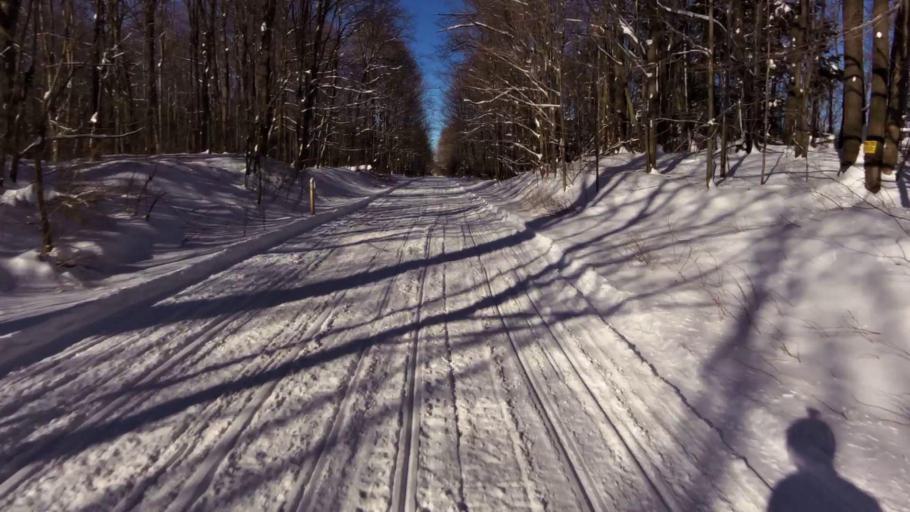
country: US
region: New York
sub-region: Chautauqua County
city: Mayville
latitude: 42.1820
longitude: -79.5803
